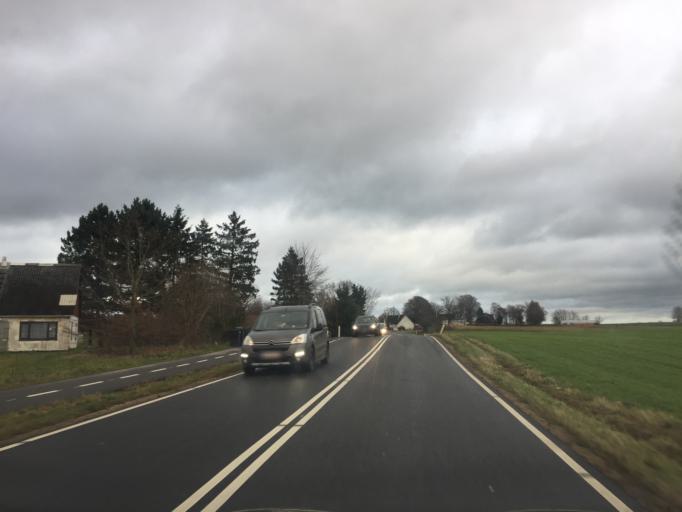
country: DK
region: Zealand
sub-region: Soro Kommune
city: Stenlille
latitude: 55.5901
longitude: 11.6677
